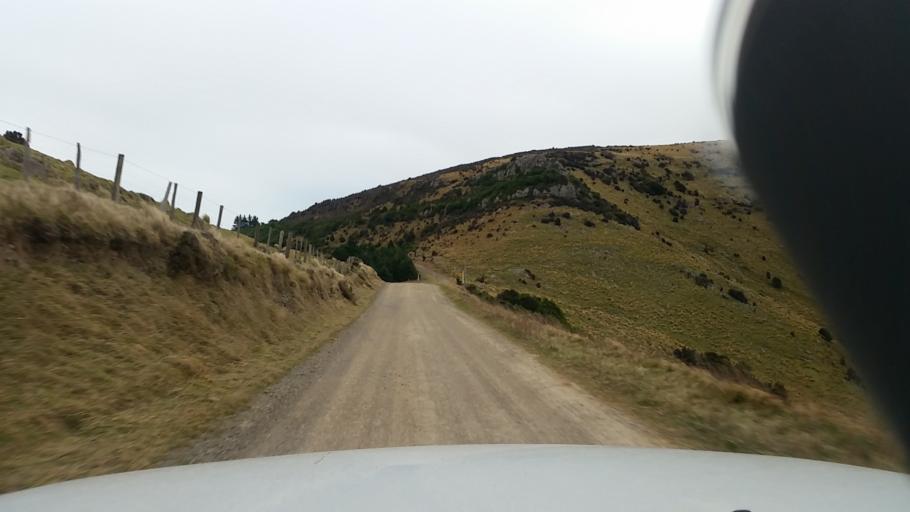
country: NZ
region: Canterbury
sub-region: Christchurch City
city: Christchurch
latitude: -43.8157
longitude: 172.7926
